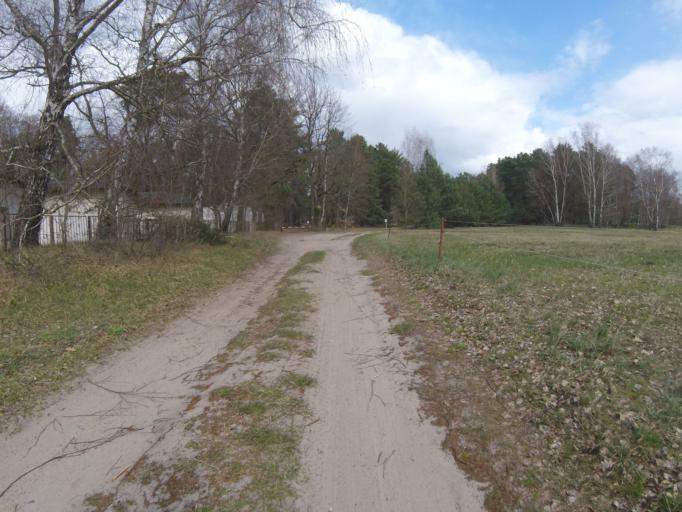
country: DE
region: Brandenburg
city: Gross Koris
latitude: 52.1850
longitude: 13.6573
